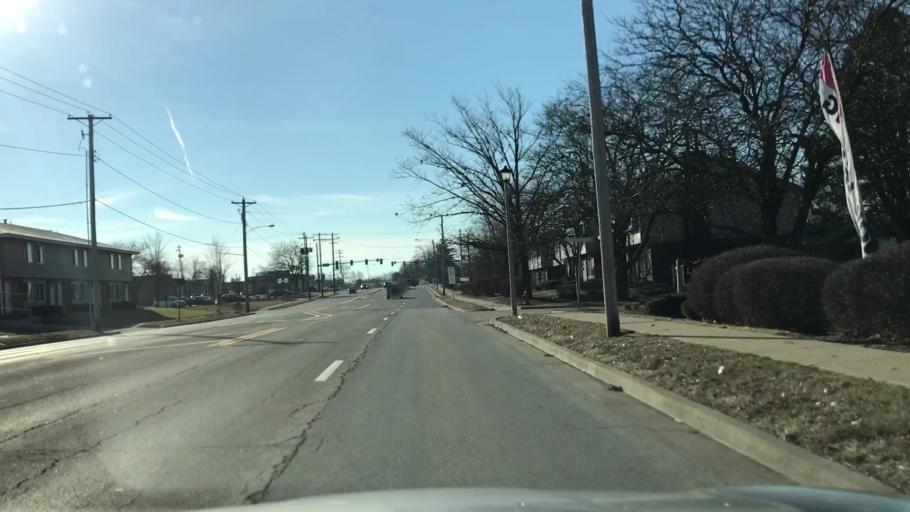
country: US
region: Illinois
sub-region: McLean County
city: Normal
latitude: 40.5123
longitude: -88.9609
